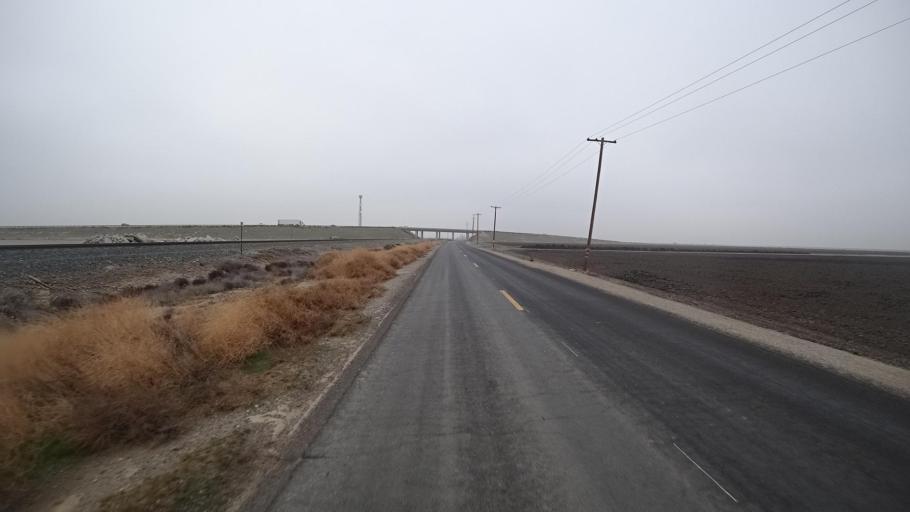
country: US
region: California
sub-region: Kern County
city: Greenfield
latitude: 35.1800
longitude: -119.1275
